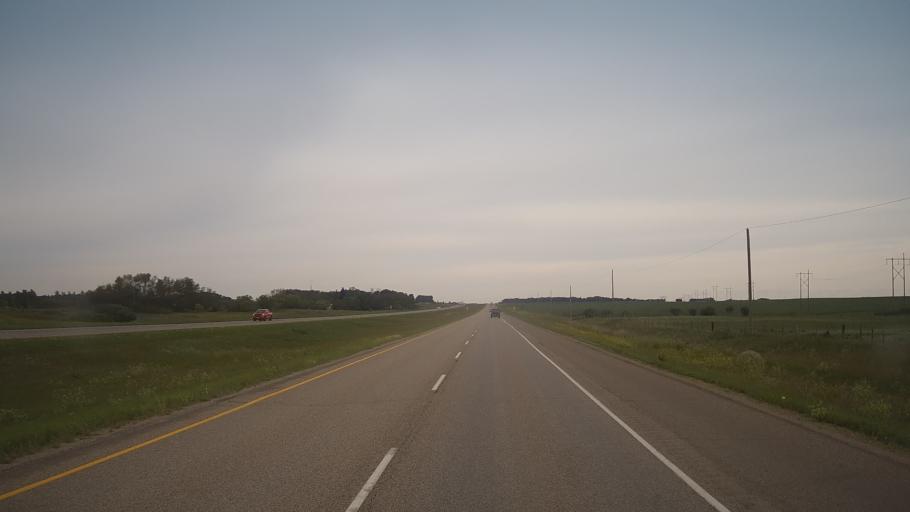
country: CA
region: Saskatchewan
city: Saskatoon
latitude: 51.8940
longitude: -106.5181
